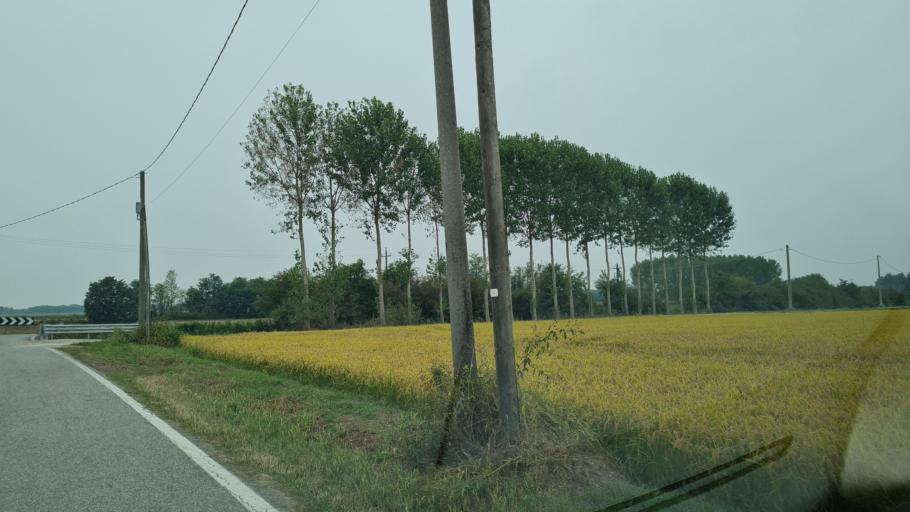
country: IT
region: Piedmont
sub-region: Provincia di Novara
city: Mandello Vitta
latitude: 45.4935
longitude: 8.4454
